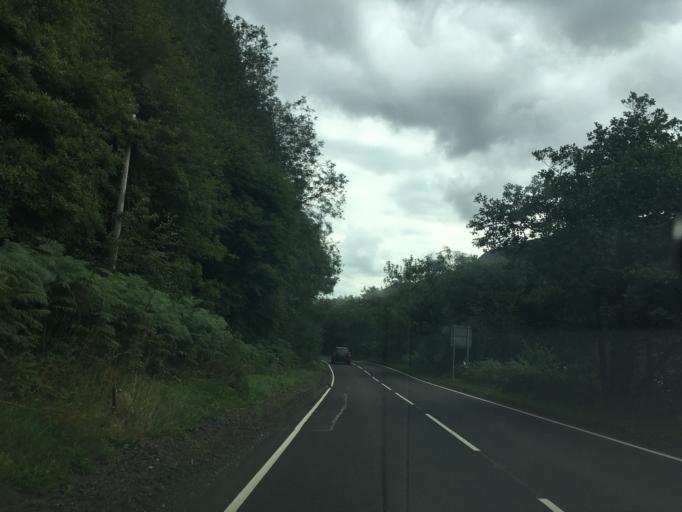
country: GB
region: Scotland
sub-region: Stirling
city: Callander
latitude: 56.3064
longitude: -4.3221
